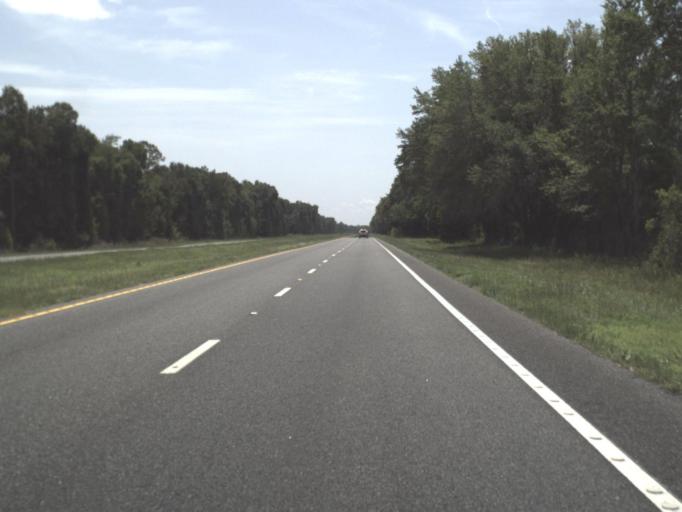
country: US
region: Florida
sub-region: Taylor County
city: Perry
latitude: 29.9624
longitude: -83.4710
